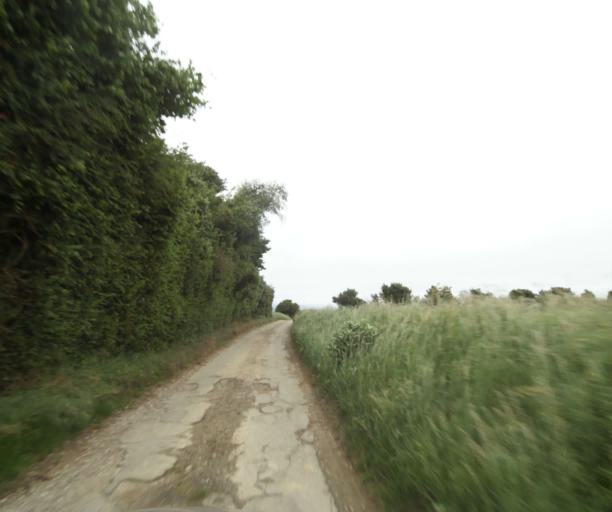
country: FR
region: Rhone-Alpes
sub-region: Departement de l'Ain
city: Miribel
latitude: 45.8480
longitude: 4.9447
